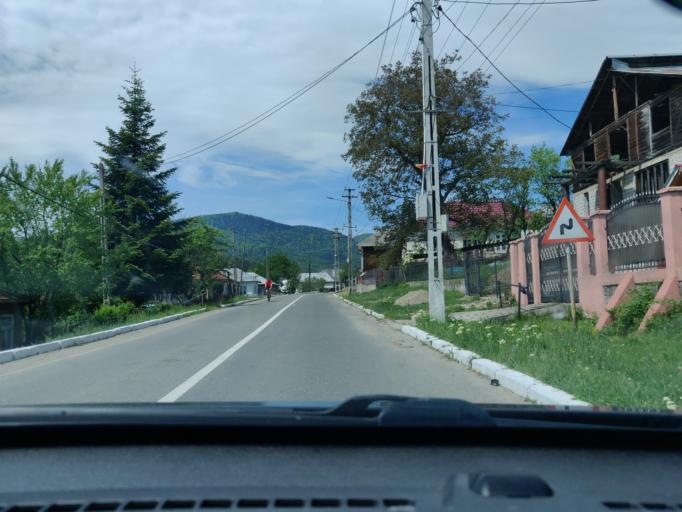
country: RO
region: Vrancea
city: Dragosloveni
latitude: 46.0003
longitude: 26.6624
